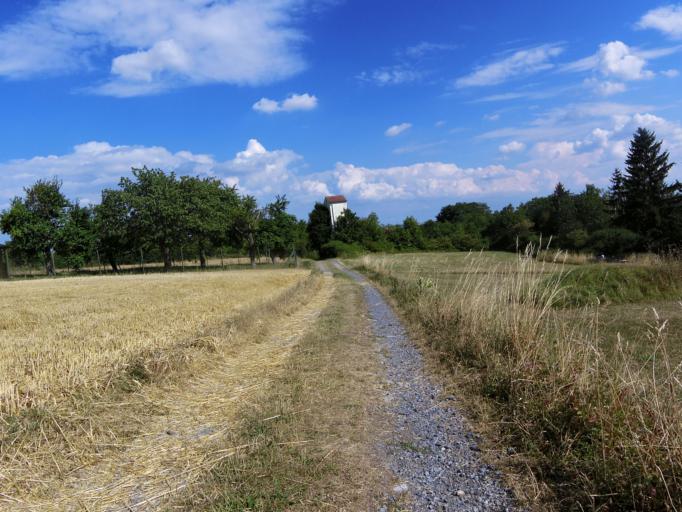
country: DE
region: Bavaria
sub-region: Regierungsbezirk Unterfranken
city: Rimpar
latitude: 49.8262
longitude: 9.9648
